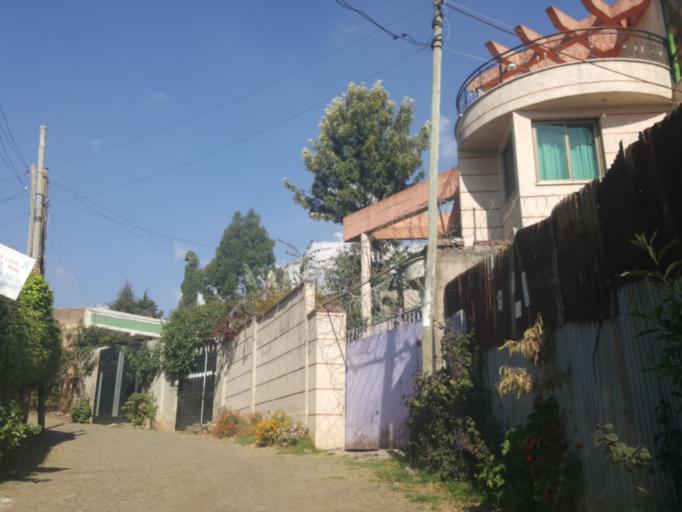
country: ET
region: Adis Abeba
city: Addis Ababa
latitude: 9.0544
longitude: 38.7278
